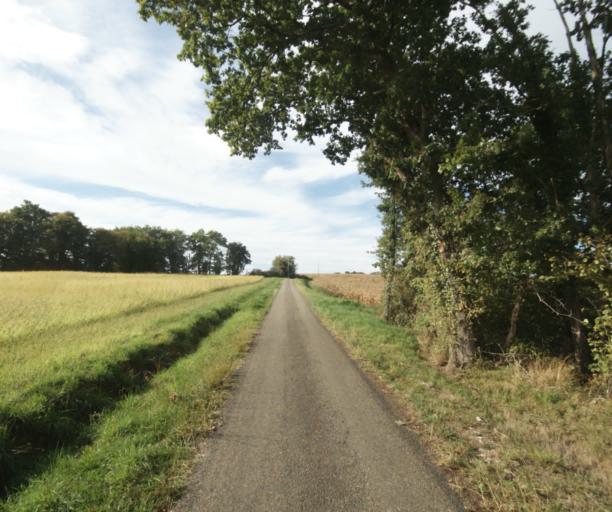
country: FR
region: Midi-Pyrenees
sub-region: Departement du Gers
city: Cazaubon
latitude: 43.8779
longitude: -0.1206
